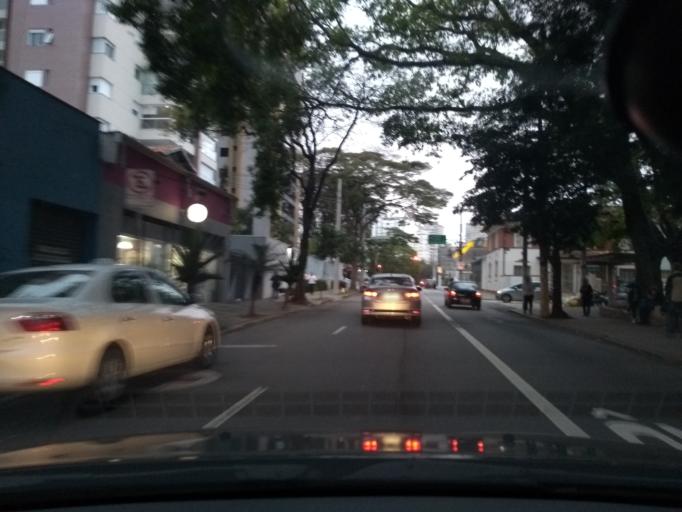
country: BR
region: Sao Paulo
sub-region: Sao Paulo
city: Sao Paulo
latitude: -23.5251
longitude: -46.6897
